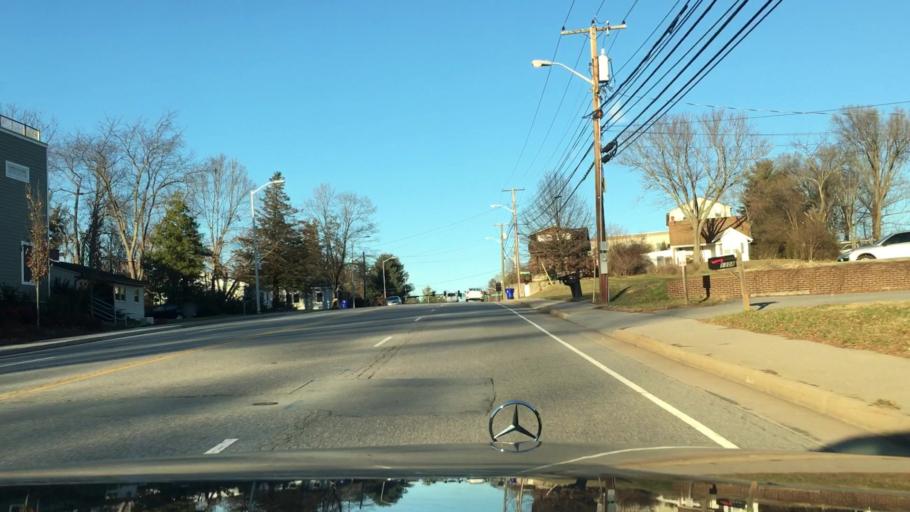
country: US
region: Virginia
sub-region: Montgomery County
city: Blacksburg
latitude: 37.2444
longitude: -80.4162
